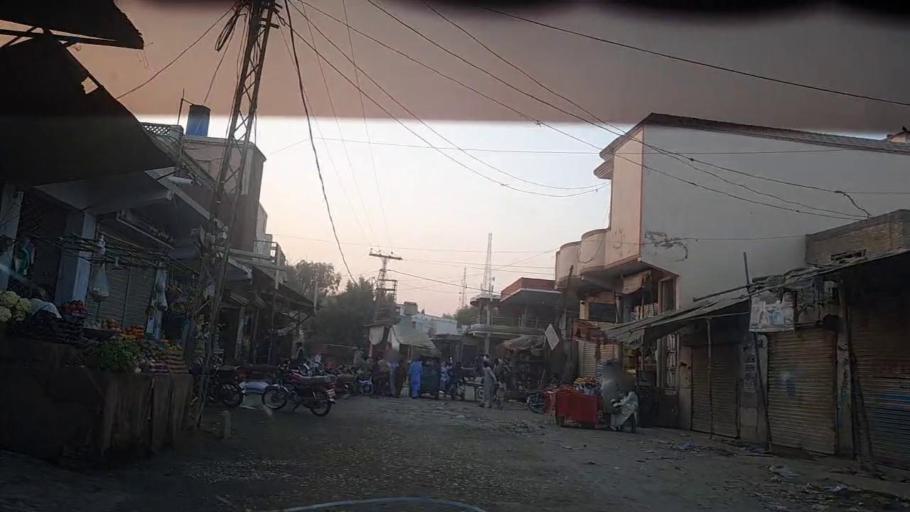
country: PK
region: Sindh
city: Ranipur
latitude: 27.2847
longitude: 68.5105
